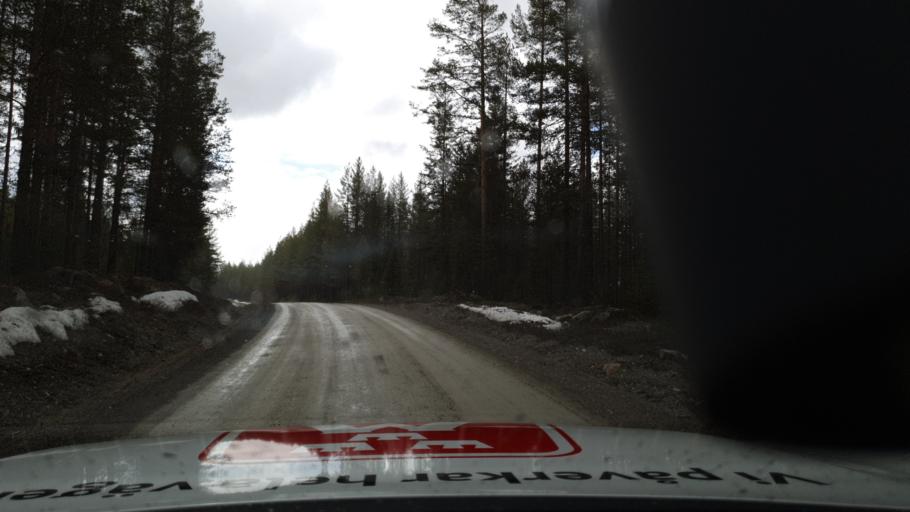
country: SE
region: Jaemtland
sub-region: Bergs Kommun
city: Hoverberg
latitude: 62.7824
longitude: 13.8241
